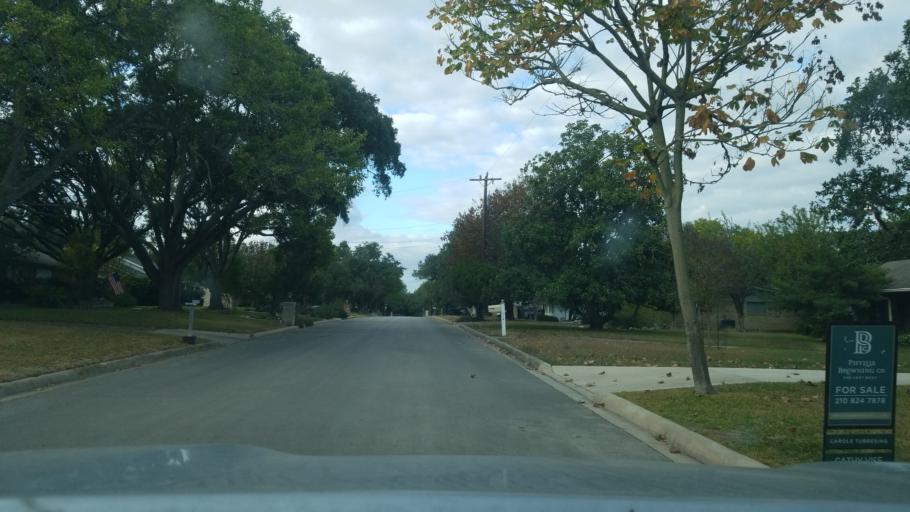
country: US
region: Texas
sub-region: Bexar County
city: Hollywood Park
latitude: 29.6018
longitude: -98.4840
